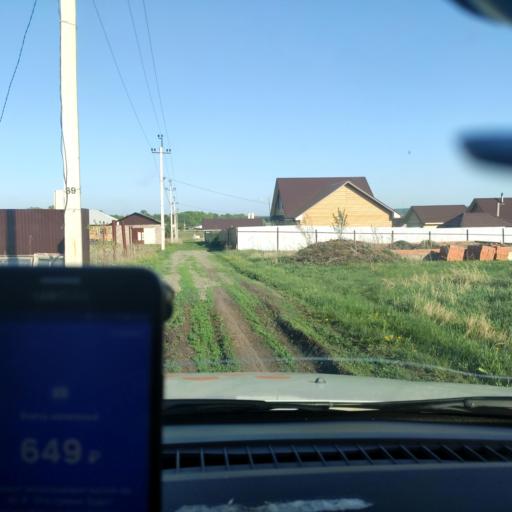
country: RU
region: Bashkortostan
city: Avdon
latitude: 54.5135
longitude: 55.8141
